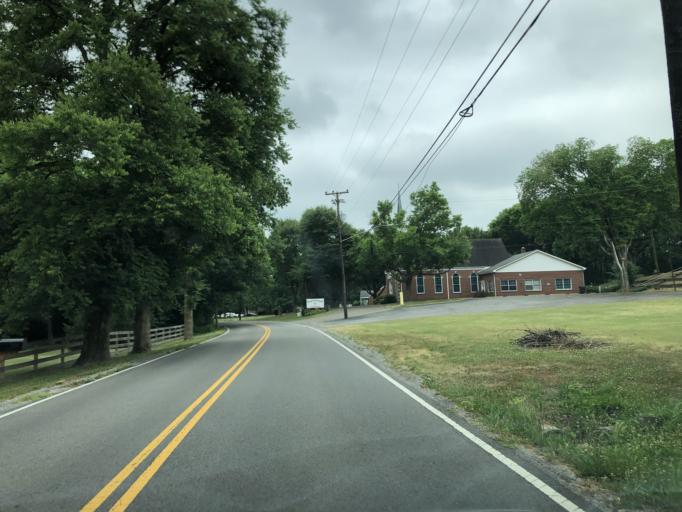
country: US
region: Tennessee
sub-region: Davidson County
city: Goodlettsville
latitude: 36.2905
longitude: -86.7796
